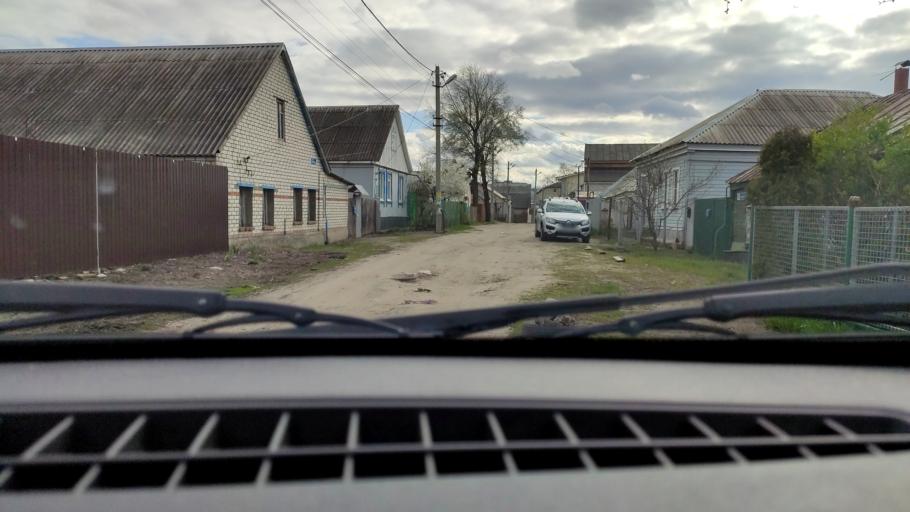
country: RU
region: Voronezj
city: Voronezh
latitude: 51.7293
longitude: 39.2649
